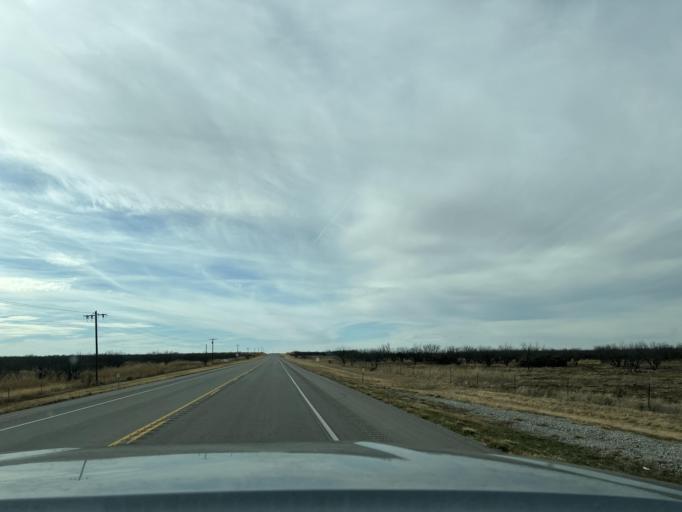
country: US
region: Texas
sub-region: Jones County
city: Anson
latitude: 32.7505
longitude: -99.6712
